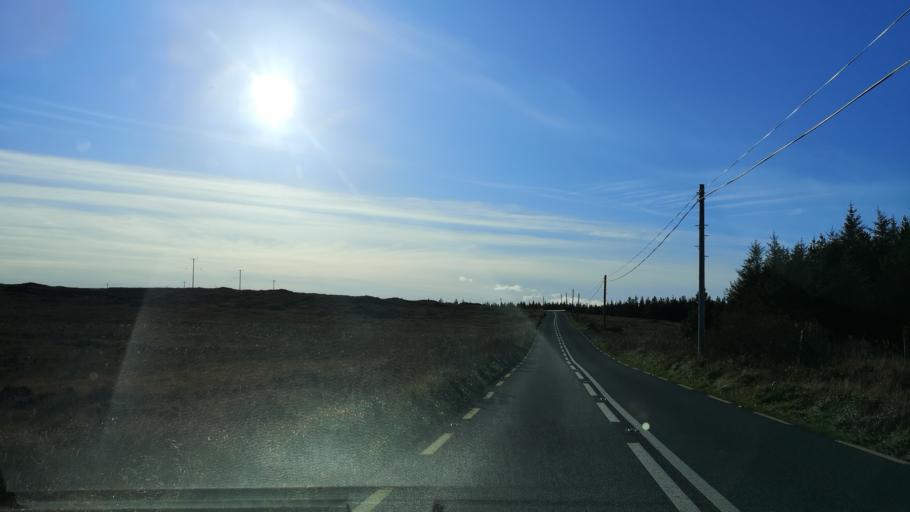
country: IE
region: Connaught
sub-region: County Galway
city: Clifden
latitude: 53.5291
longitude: -10.0443
